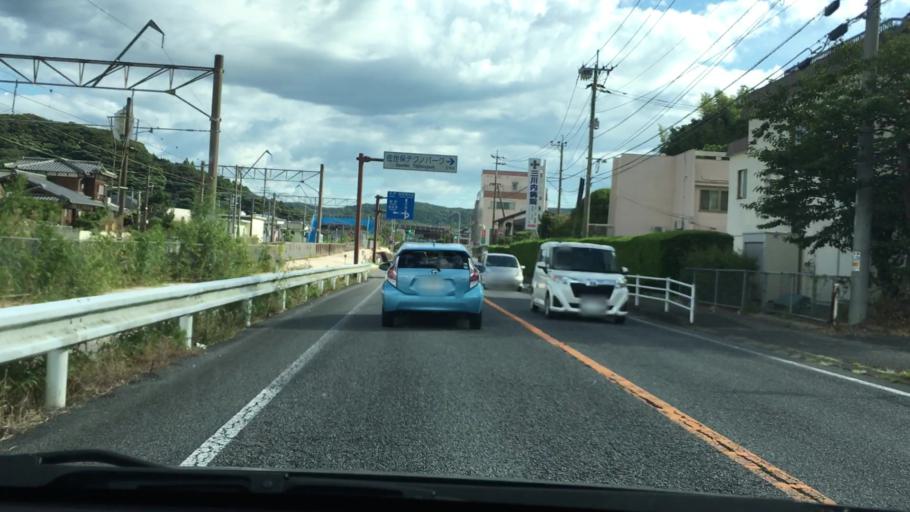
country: JP
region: Nagasaki
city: Sasebo
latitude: 33.1518
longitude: 129.8296
